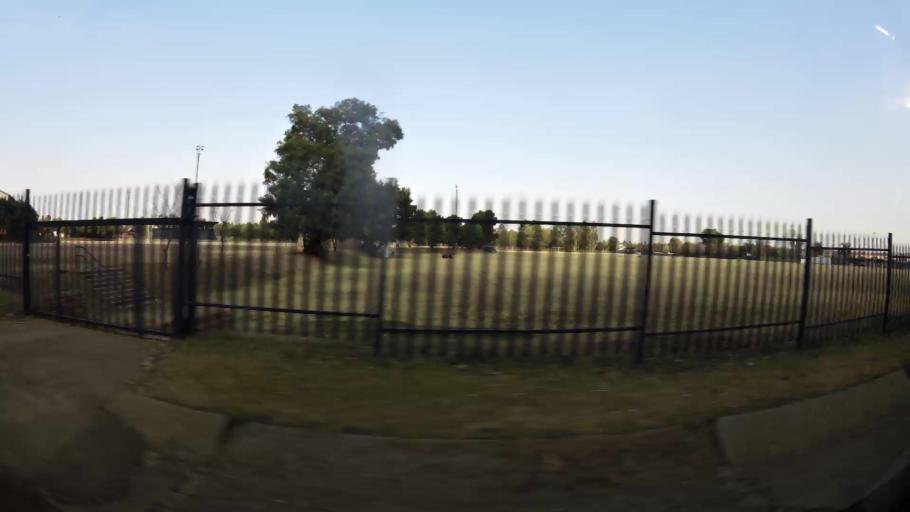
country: ZA
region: Gauteng
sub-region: Ekurhuleni Metropolitan Municipality
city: Benoni
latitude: -26.1093
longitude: 28.3711
